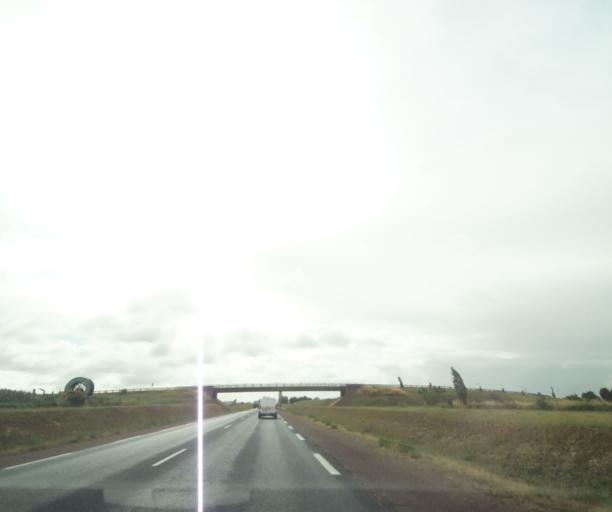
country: FR
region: Pays de la Loire
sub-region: Departement de la Vendee
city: Lucon
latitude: 46.4723
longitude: -1.1684
